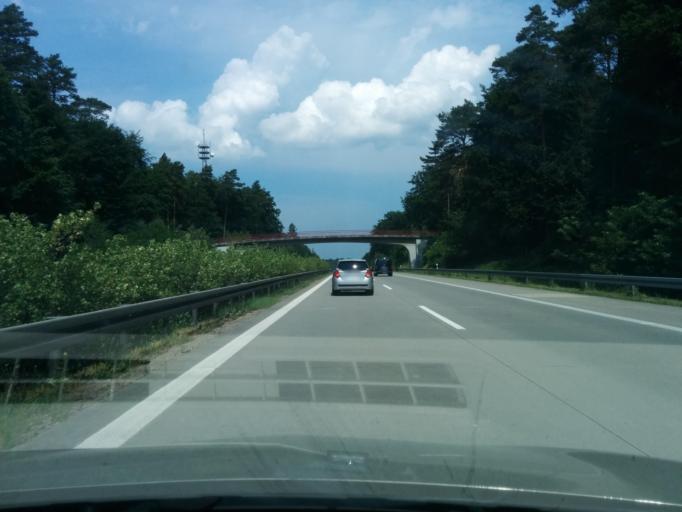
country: DE
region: Brandenburg
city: Bernau bei Berlin
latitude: 52.7427
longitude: 13.5414
